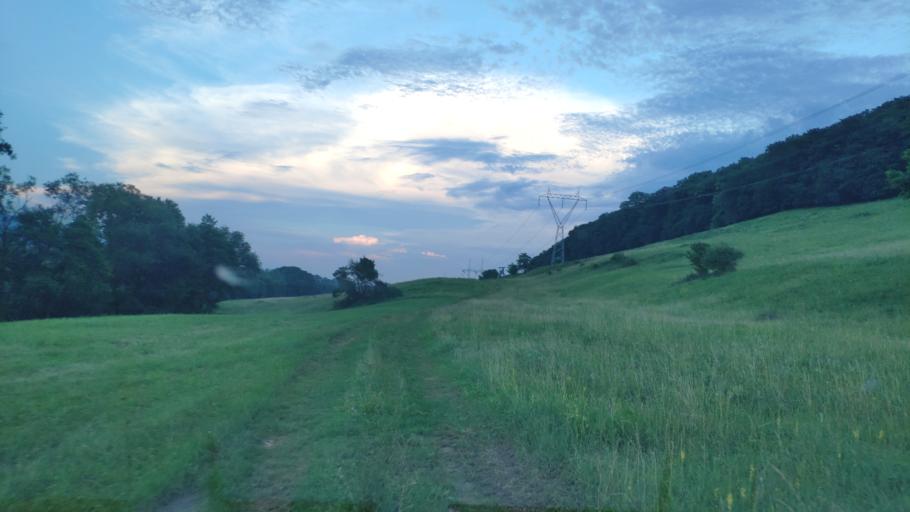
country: HU
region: Borsod-Abauj-Zemplen
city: Szendro
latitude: 48.5850
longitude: 20.7413
